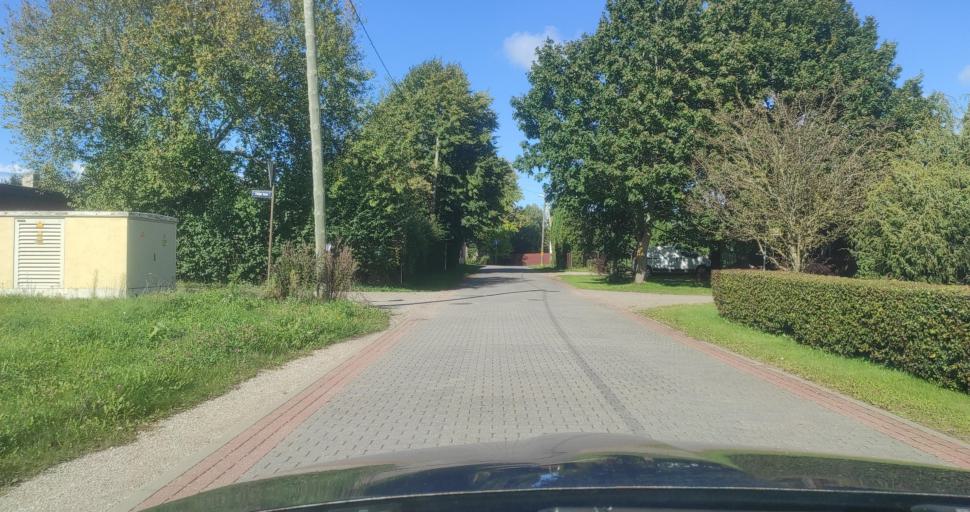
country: LV
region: Ventspils
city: Ventspils
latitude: 57.3852
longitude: 21.6104
